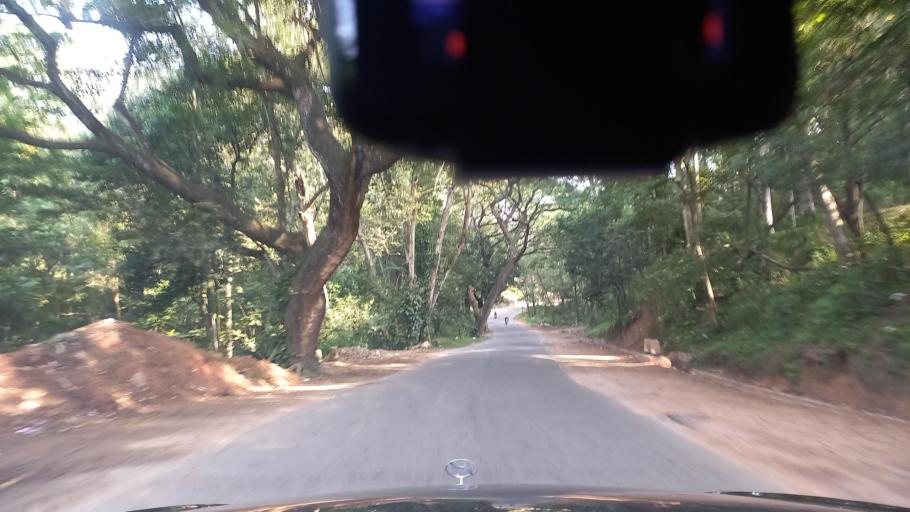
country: LK
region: Central
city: Kandy
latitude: 7.2462
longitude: 80.5983
